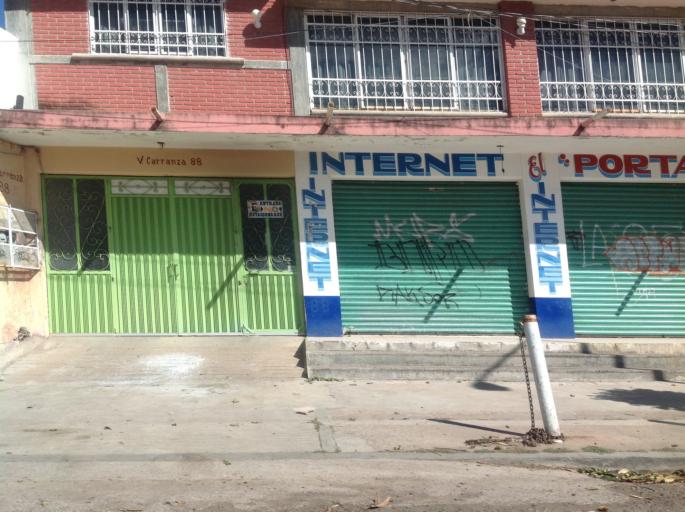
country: MX
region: Oaxaca
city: Ciudad de Huajuapam de Leon
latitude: 17.8121
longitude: -97.7691
